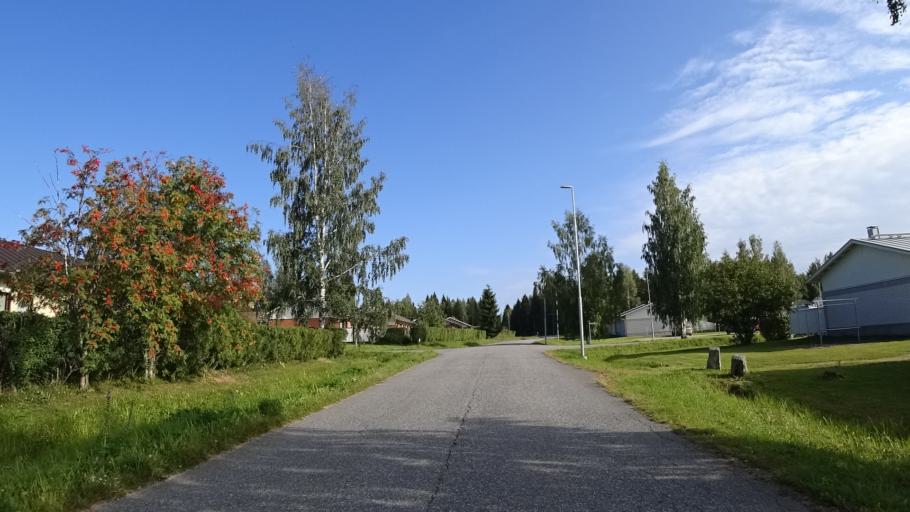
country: FI
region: North Karelia
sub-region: Joensuu
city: Eno
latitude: 62.7947
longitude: 30.1405
